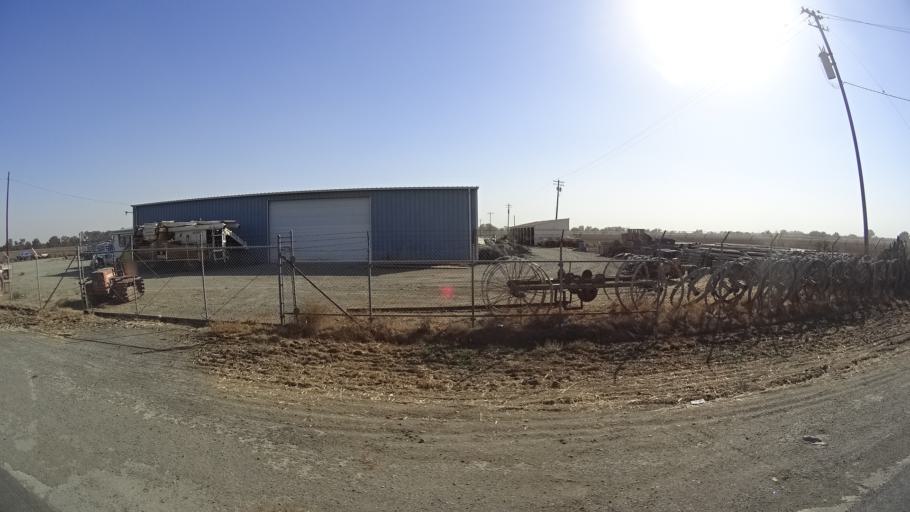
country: US
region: California
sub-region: Yolo County
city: Woodland
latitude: 38.7352
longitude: -121.7742
